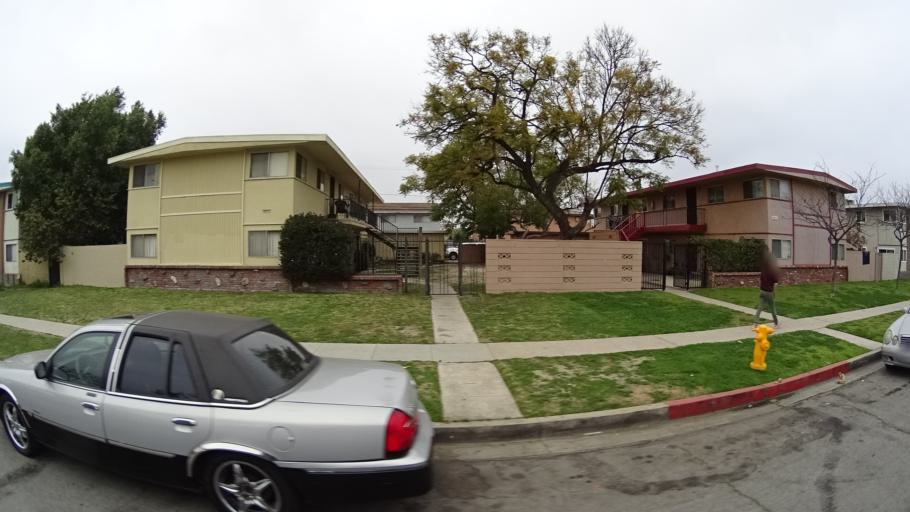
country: US
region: California
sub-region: Orange County
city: Stanton
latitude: 33.8269
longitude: -118.0092
